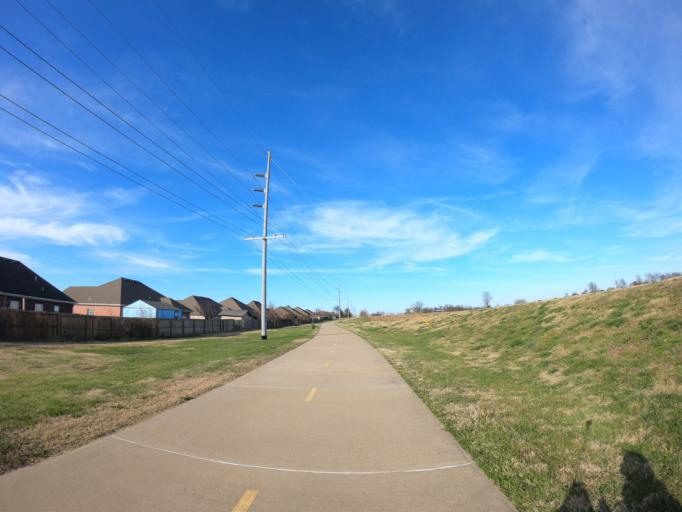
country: US
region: Arkansas
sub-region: Benton County
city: Lowell
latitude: 36.2707
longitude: -94.1676
